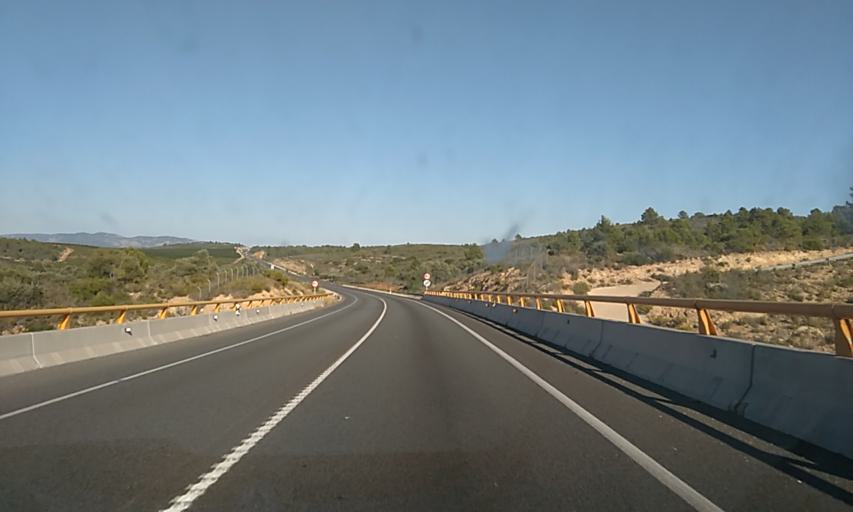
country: ES
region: Valencia
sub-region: Provincia de Castello
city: Torreblanca
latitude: 40.2102
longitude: 0.1399
